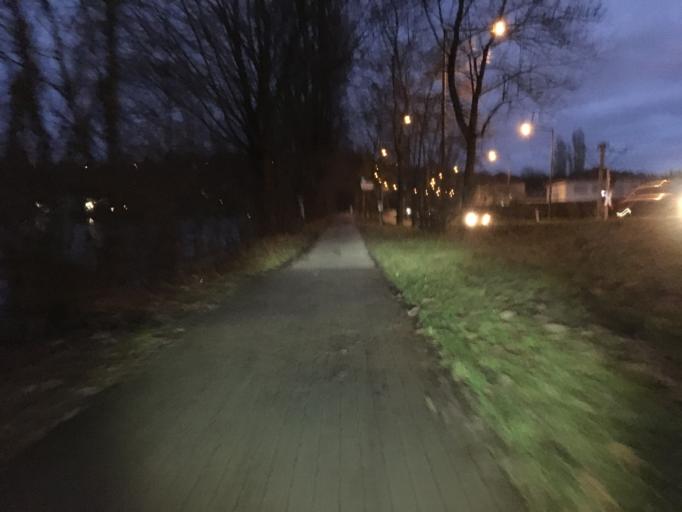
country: DE
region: Baden-Wuerttemberg
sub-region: Regierungsbezirk Stuttgart
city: Stuttgart Muehlhausen
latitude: 48.8260
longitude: 9.2131
